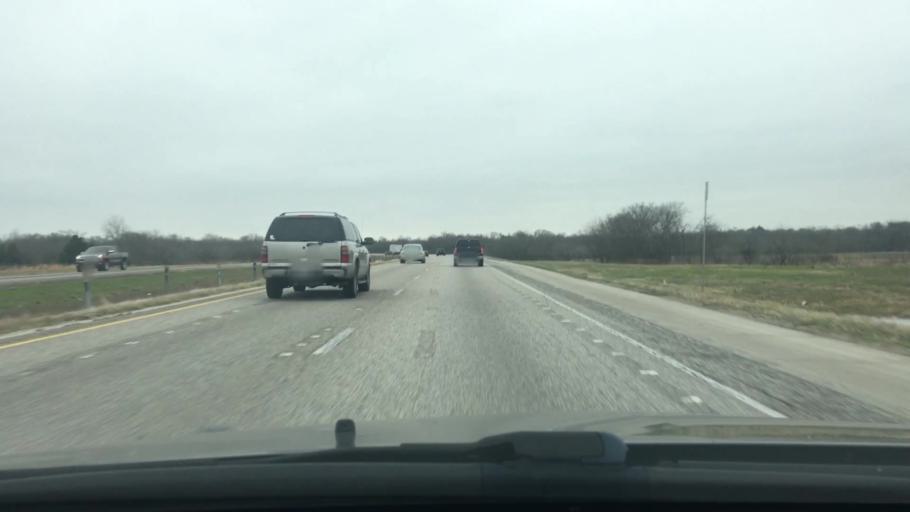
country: US
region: Texas
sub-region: Freestone County
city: Wortham
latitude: 31.8726
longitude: -96.3386
